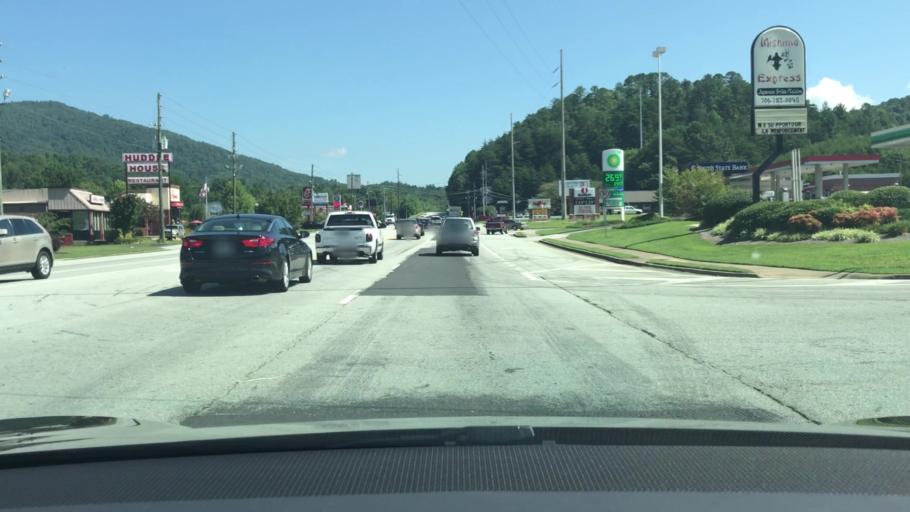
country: US
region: Georgia
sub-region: Rabun County
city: Clayton
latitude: 34.8792
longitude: -83.3967
